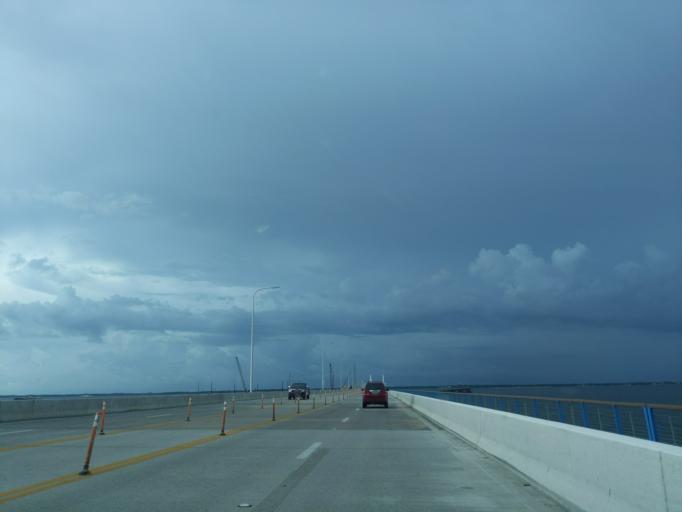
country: US
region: Florida
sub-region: Escambia County
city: East Pensacola Heights
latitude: 30.4053
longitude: -87.1896
